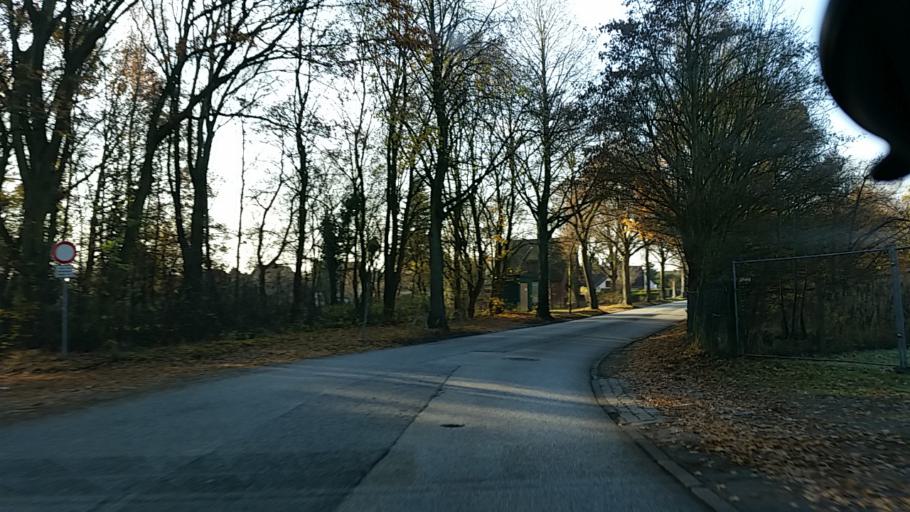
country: DE
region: Schleswig-Holstein
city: Oststeinbek
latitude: 53.5423
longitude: 10.1518
